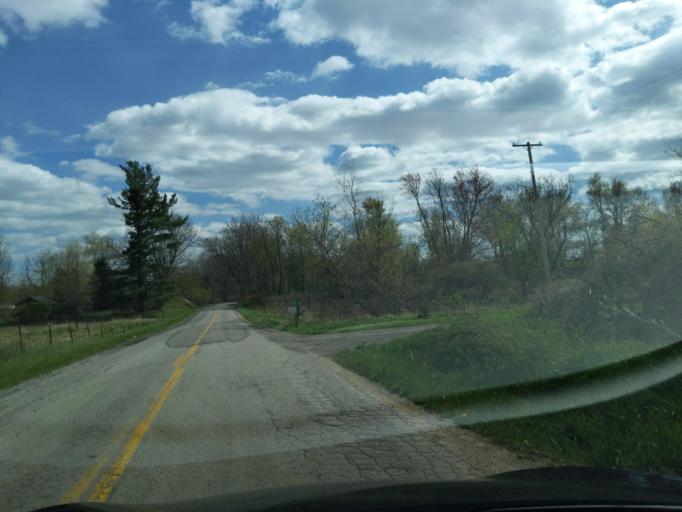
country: US
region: Michigan
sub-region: Ingham County
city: Leslie
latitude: 42.4628
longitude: -84.5411
